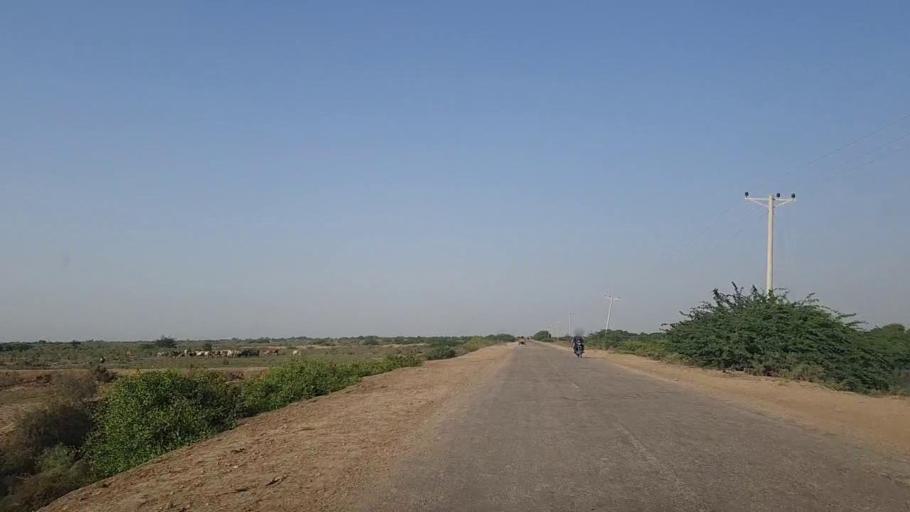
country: PK
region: Sindh
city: Mirpur Batoro
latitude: 24.6060
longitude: 68.4021
